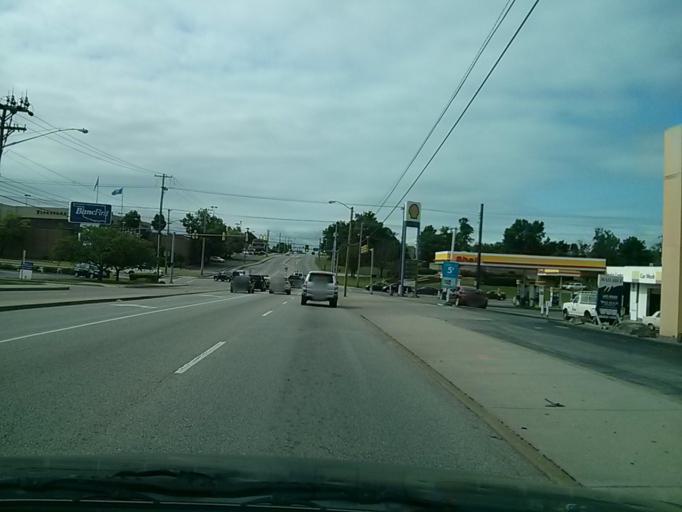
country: US
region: Oklahoma
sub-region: Tulsa County
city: Tulsa
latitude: 36.1053
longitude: -95.9225
